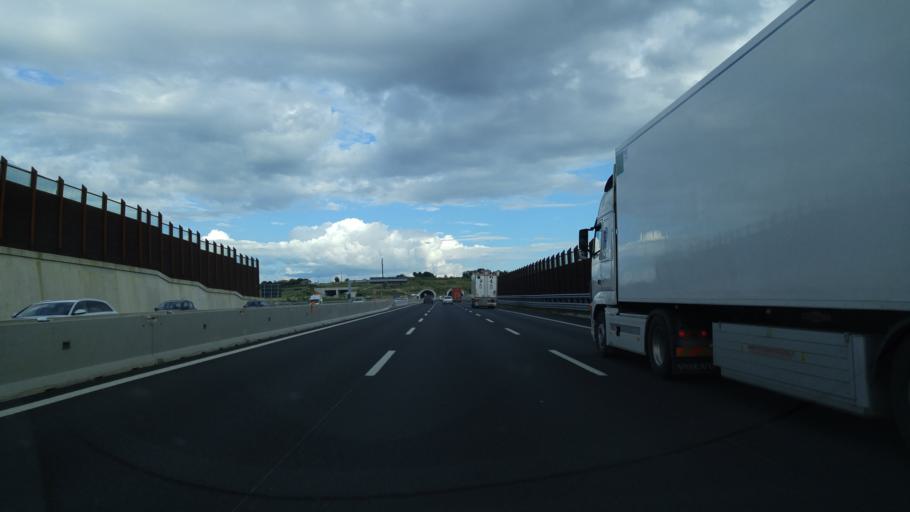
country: IT
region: Emilia-Romagna
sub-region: Provincia di Rimini
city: Riccione
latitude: 43.9824
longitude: 12.6480
